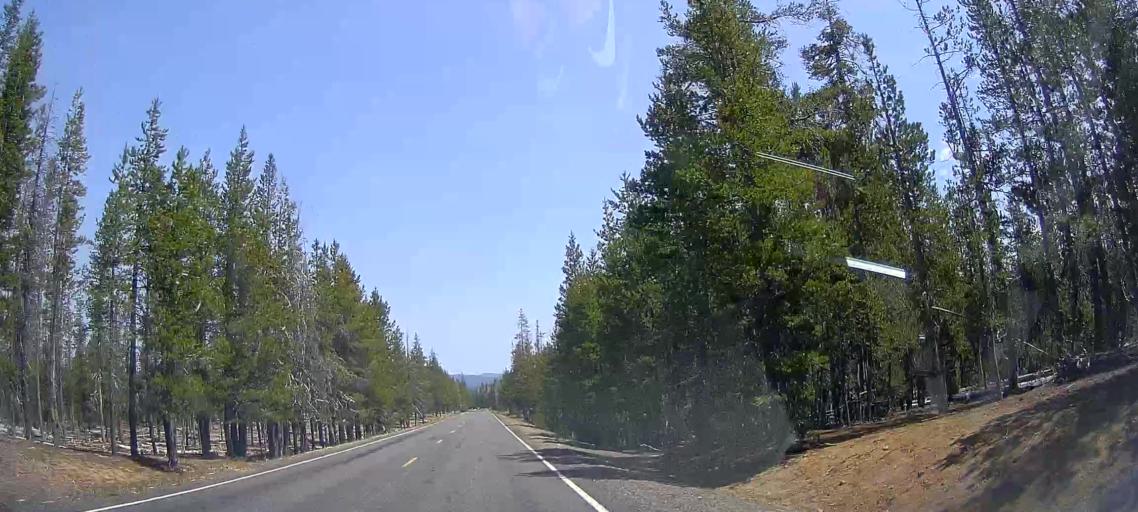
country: US
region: Oregon
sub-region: Jackson County
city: Shady Cove
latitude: 43.0198
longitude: -122.1239
